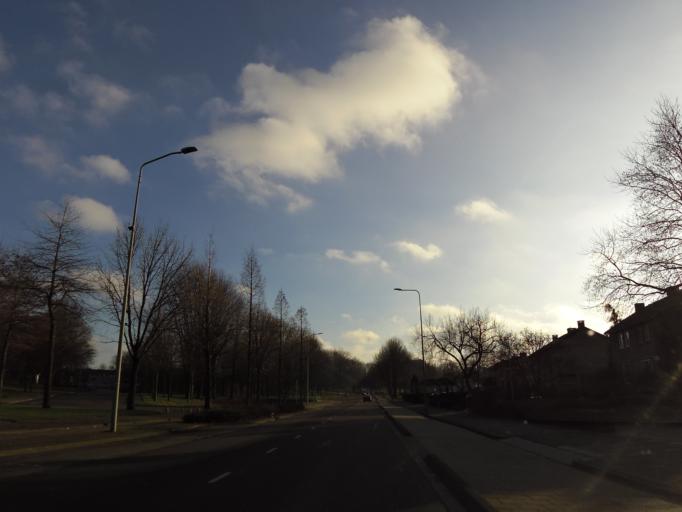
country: NL
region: Limburg
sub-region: Gemeente Heerlen
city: Heerlen
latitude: 50.8964
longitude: 5.9830
